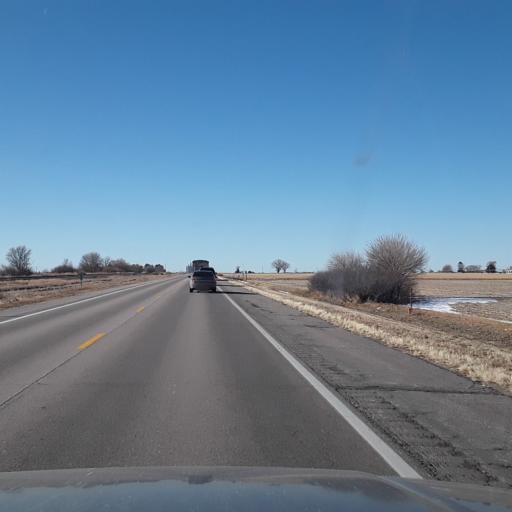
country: US
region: Nebraska
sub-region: Kearney County
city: Minden
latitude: 40.4992
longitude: -98.9772
